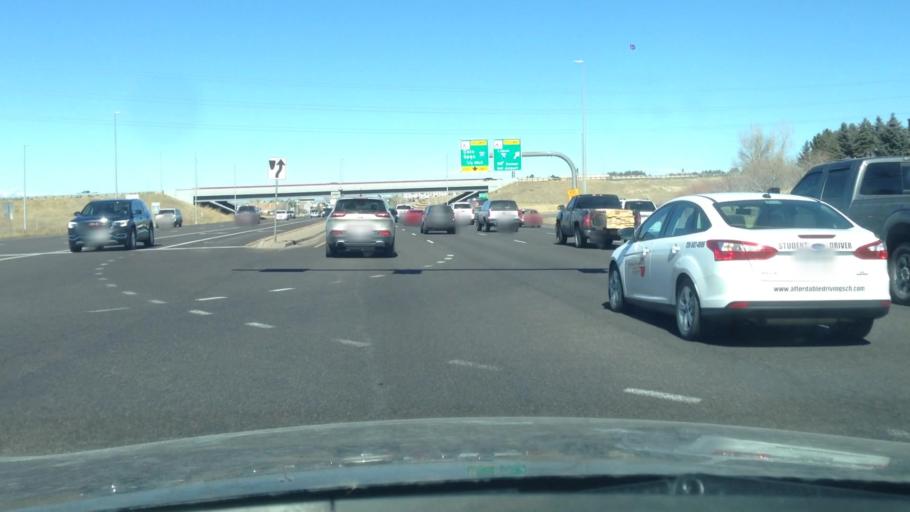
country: US
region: Colorado
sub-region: Douglas County
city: Parker
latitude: 39.5496
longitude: -104.7749
